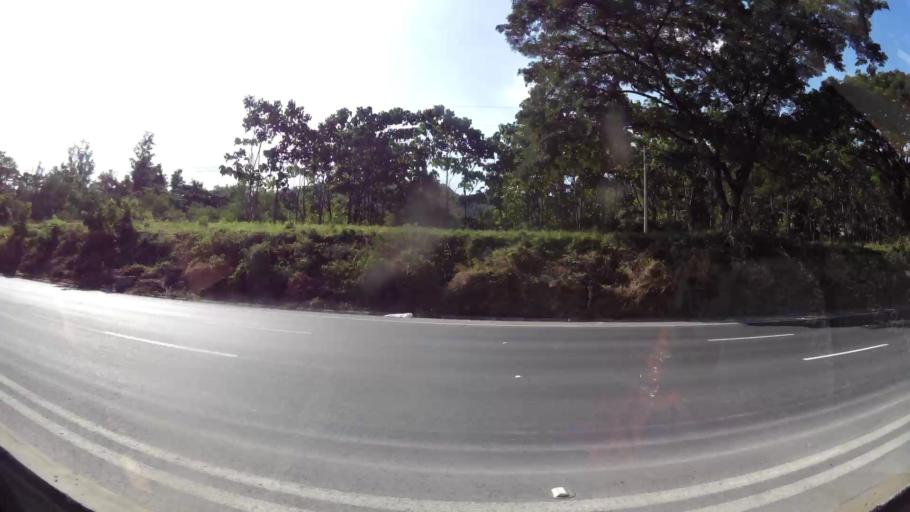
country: EC
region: Guayas
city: Santa Lucia
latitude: -2.1860
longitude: -80.0122
